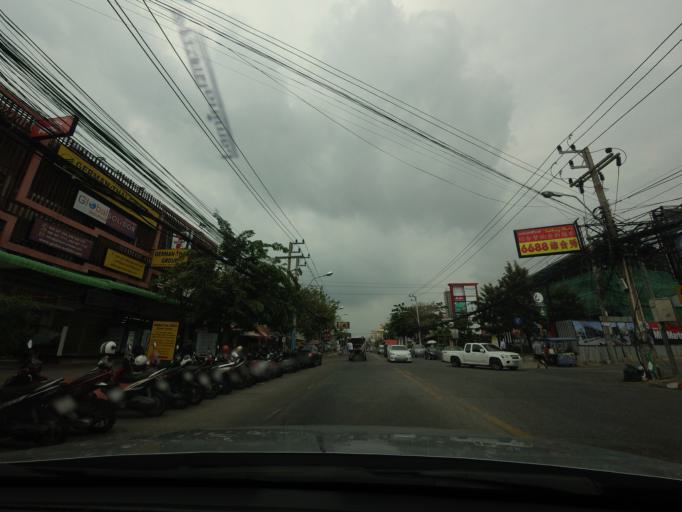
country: TH
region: Chon Buri
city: Phatthaya
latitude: 12.9538
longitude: 100.8898
